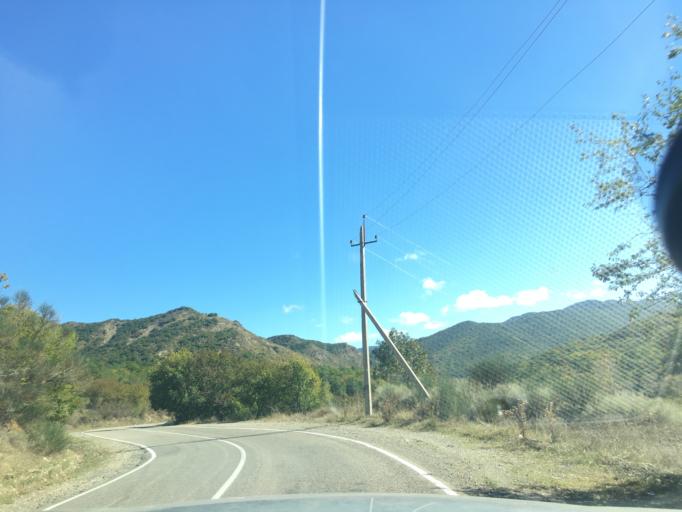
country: GE
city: Zahesi
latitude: 41.8376
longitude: 44.8669
